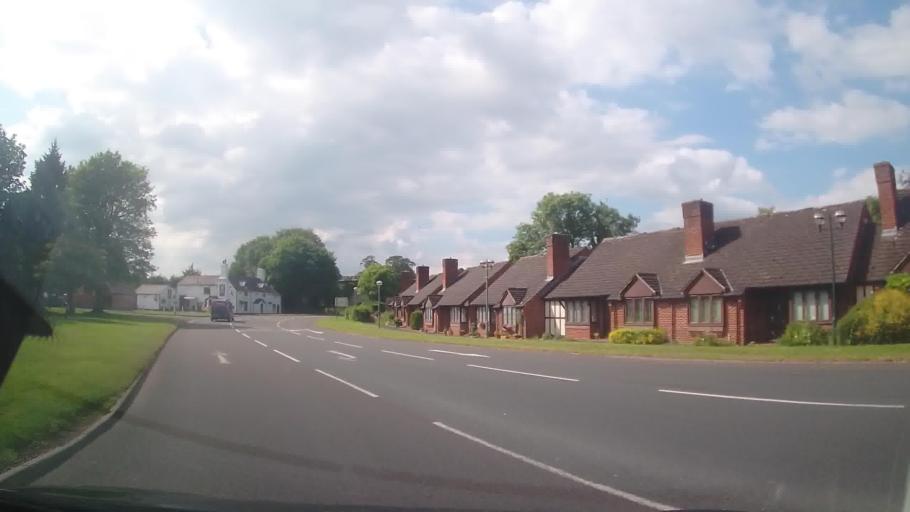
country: GB
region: England
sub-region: Shropshire
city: Whittington
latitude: 52.8726
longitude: -3.0004
